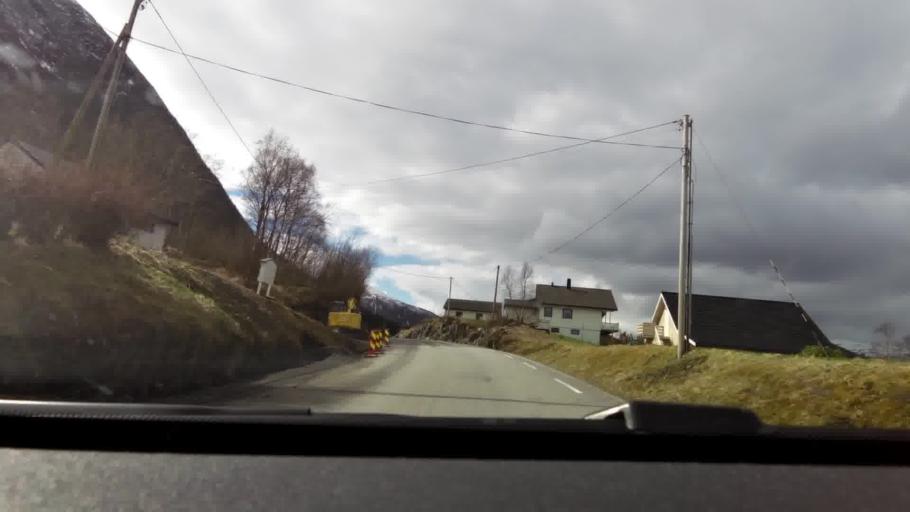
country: NO
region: More og Romsdal
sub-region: Gjemnes
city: Batnfjordsora
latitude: 62.9243
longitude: 7.5700
